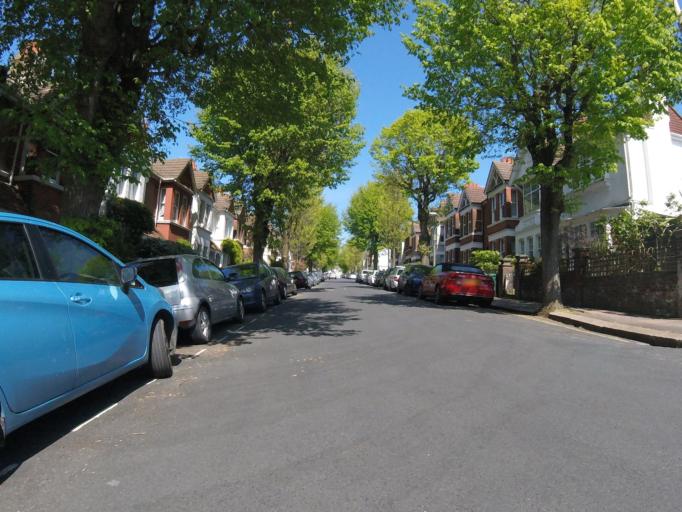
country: GB
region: England
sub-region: Brighton and Hove
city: Brighton
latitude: 50.8454
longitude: -0.1393
